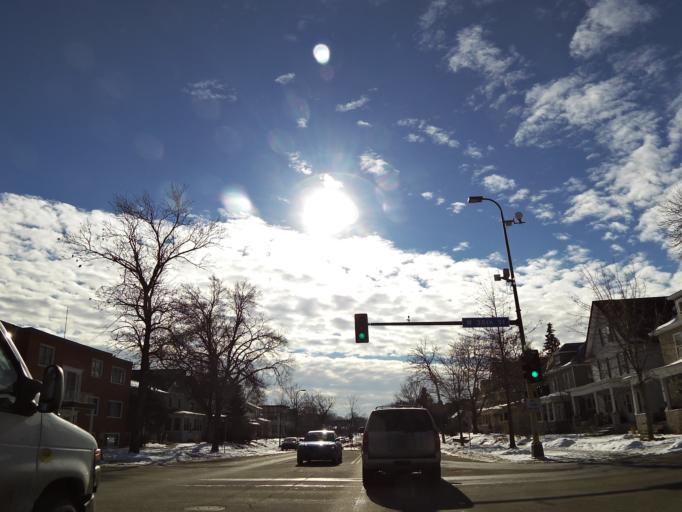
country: US
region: Minnesota
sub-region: Hennepin County
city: Minneapolis
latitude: 44.9396
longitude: -93.2882
